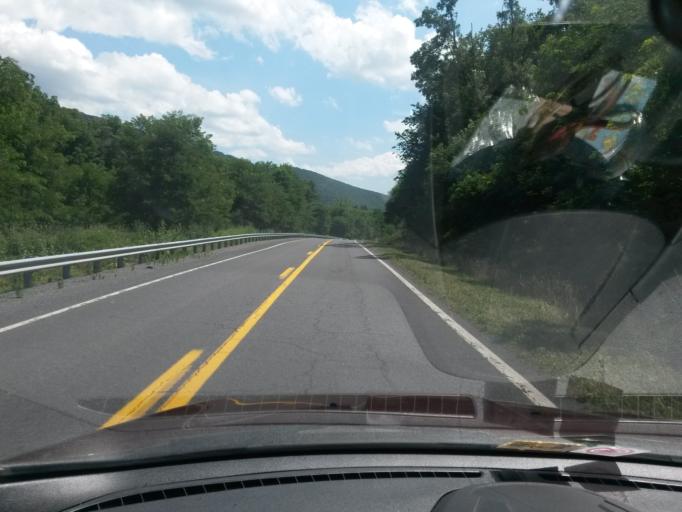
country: US
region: West Virginia
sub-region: Pendleton County
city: Franklin
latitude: 38.7493
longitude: -79.2868
